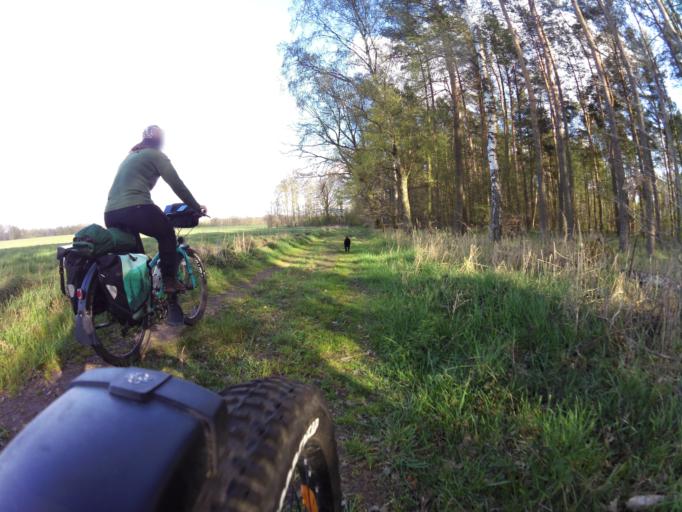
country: PL
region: West Pomeranian Voivodeship
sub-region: Powiat gryficki
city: Ploty
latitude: 53.7668
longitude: 15.2575
